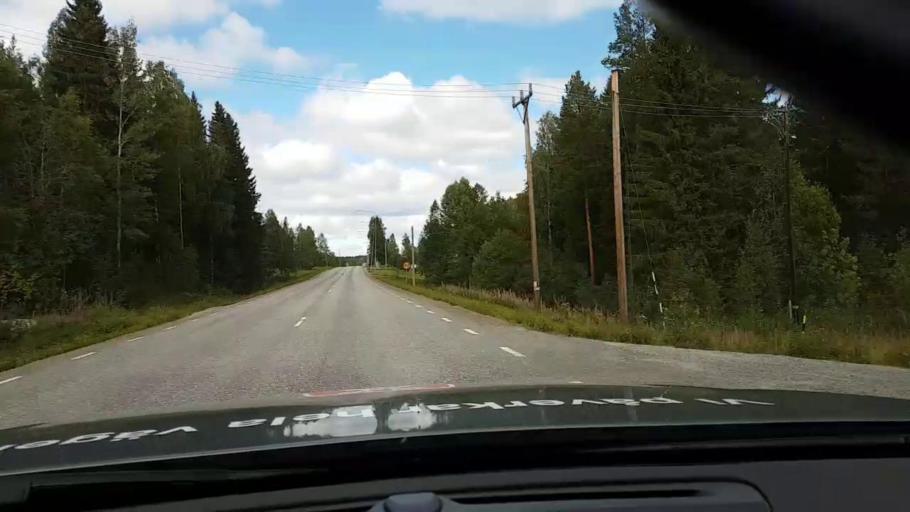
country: SE
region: Vaesternorrland
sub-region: OErnskoeldsviks Kommun
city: Bredbyn
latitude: 63.4743
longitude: 18.0965
